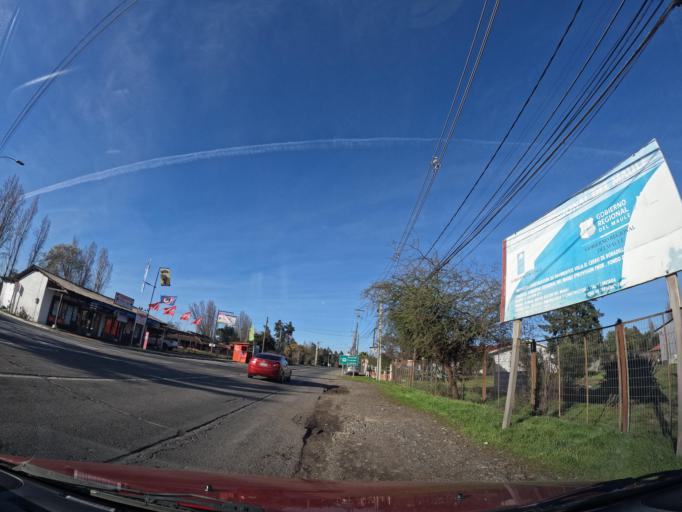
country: CL
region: Maule
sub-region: Provincia de Linares
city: San Javier
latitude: -35.5719
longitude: -71.6891
